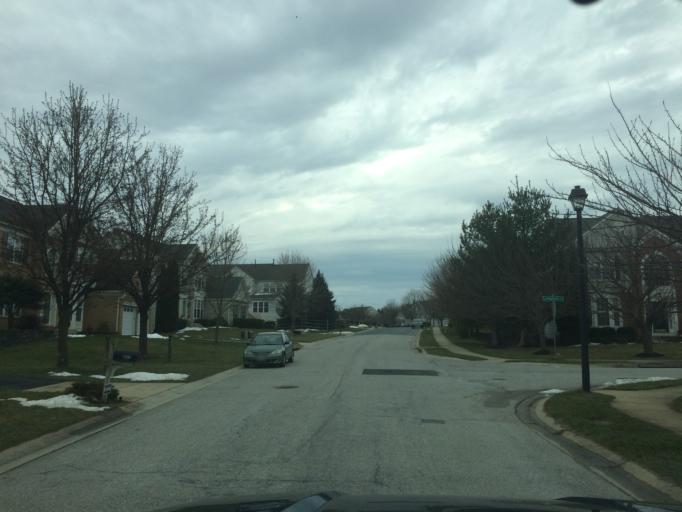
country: US
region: Maryland
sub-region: Howard County
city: Highland
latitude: 39.2014
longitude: -76.9349
